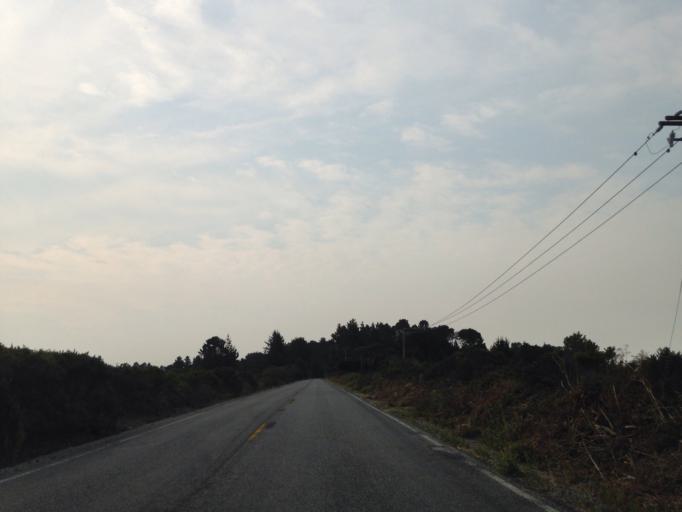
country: US
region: California
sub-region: San Mateo County
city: Highlands-Baywood Park
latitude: 37.4758
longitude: -122.3582
